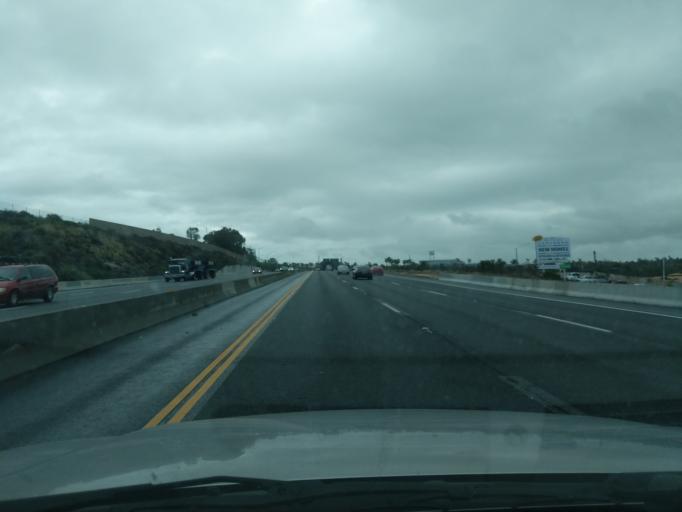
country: US
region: California
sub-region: San Diego County
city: Carlsbad
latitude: 33.1813
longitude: -117.3038
